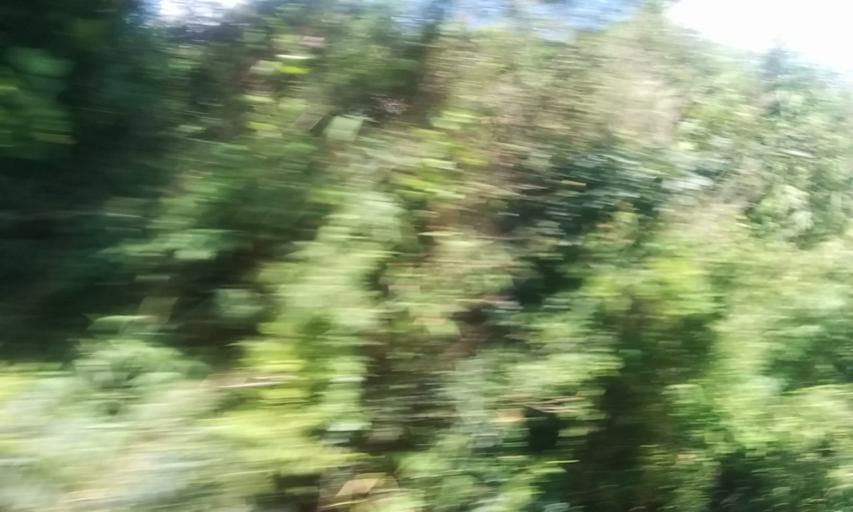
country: JP
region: Chiba
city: Oami
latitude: 35.5323
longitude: 140.2661
